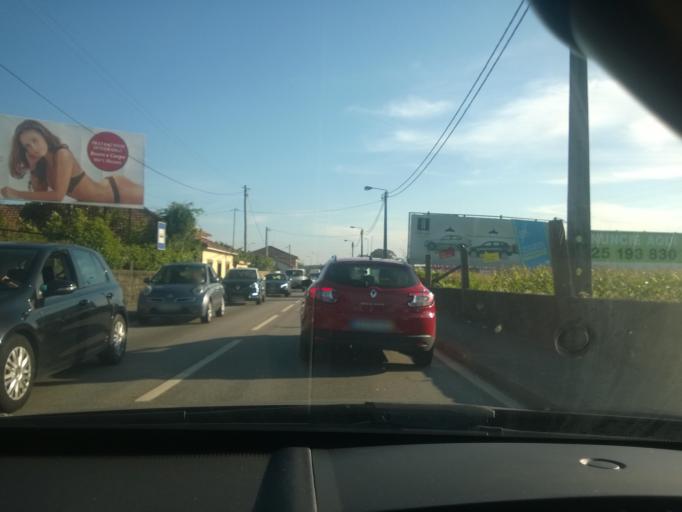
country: PT
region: Porto
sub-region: Maia
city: Anta
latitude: 41.2560
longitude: -8.6164
